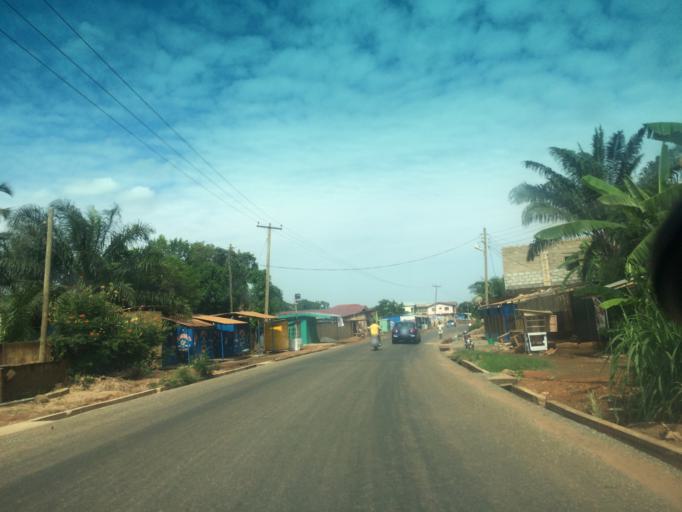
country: GH
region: Greater Accra
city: Medina Estates
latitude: 5.7423
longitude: -0.1740
